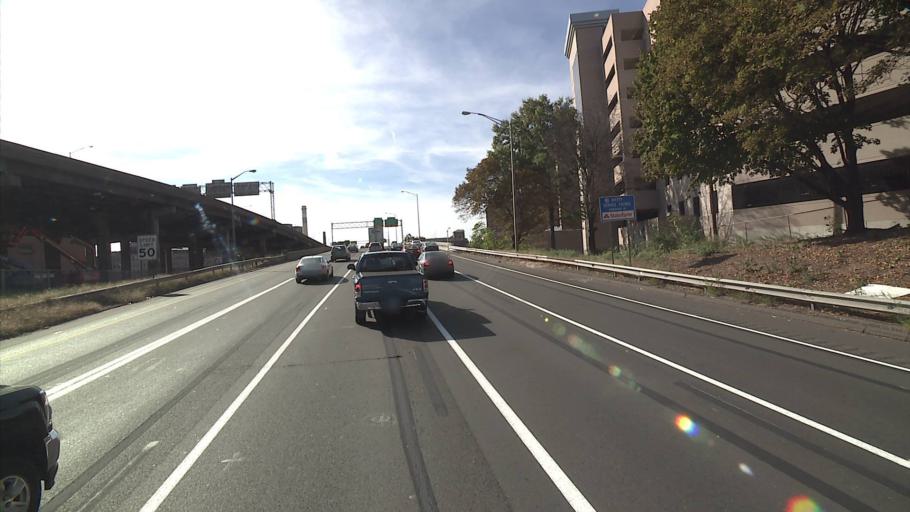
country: US
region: Connecticut
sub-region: Hartford County
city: Hartford
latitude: 41.7665
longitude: -72.6870
